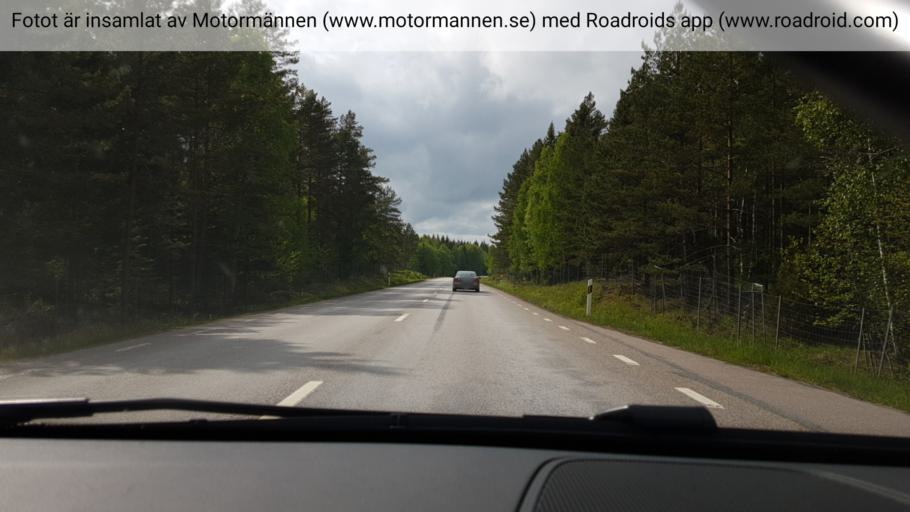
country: SE
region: Uppsala
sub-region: Osthammars Kommun
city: Osterbybruk
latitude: 60.1708
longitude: 17.9382
